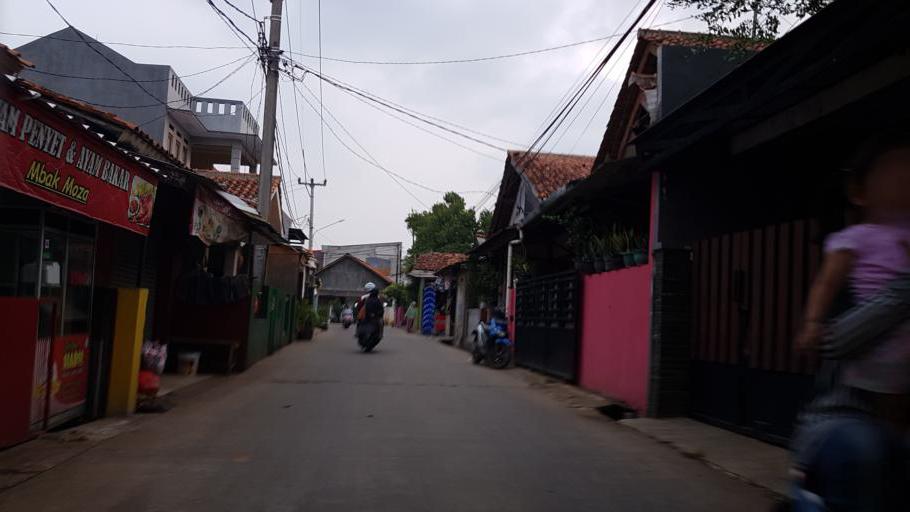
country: ID
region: West Java
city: Sawangan
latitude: -6.3773
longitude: 106.7946
